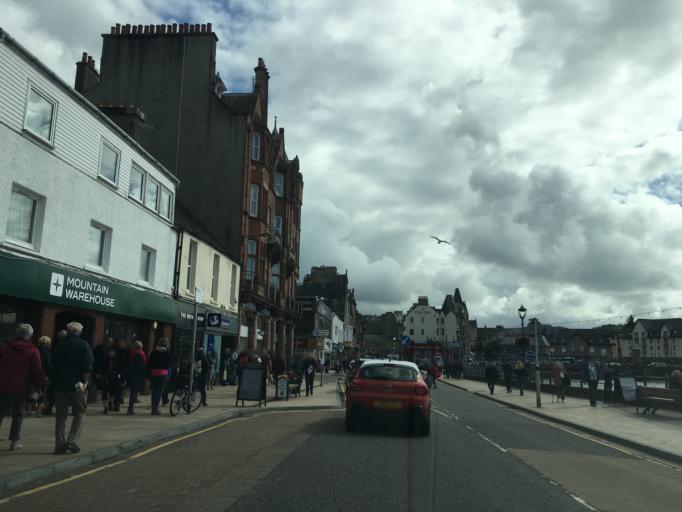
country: GB
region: Scotland
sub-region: Argyll and Bute
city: Oban
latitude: 56.4147
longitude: -5.4727
